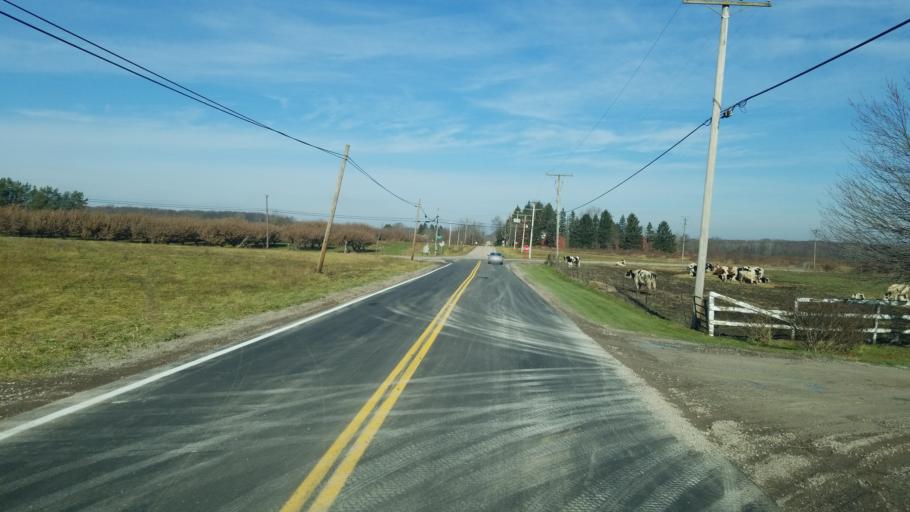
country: US
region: Ohio
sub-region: Ashtabula County
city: Geneva
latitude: 41.7293
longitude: -80.9033
